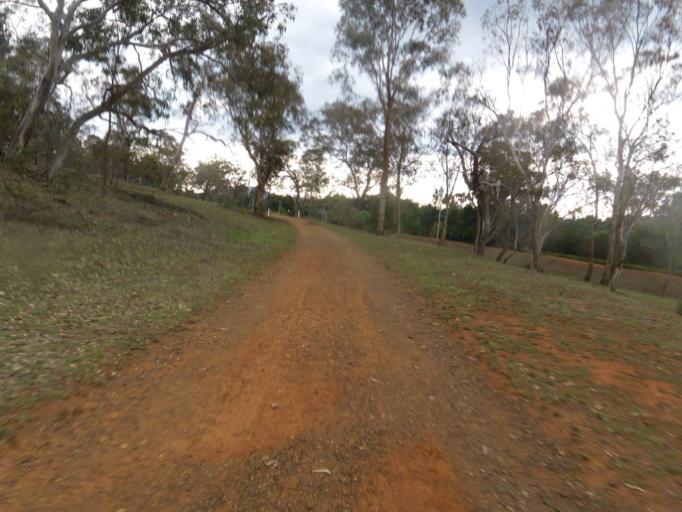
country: AU
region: Australian Capital Territory
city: Forrest
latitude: -35.3274
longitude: 149.1204
